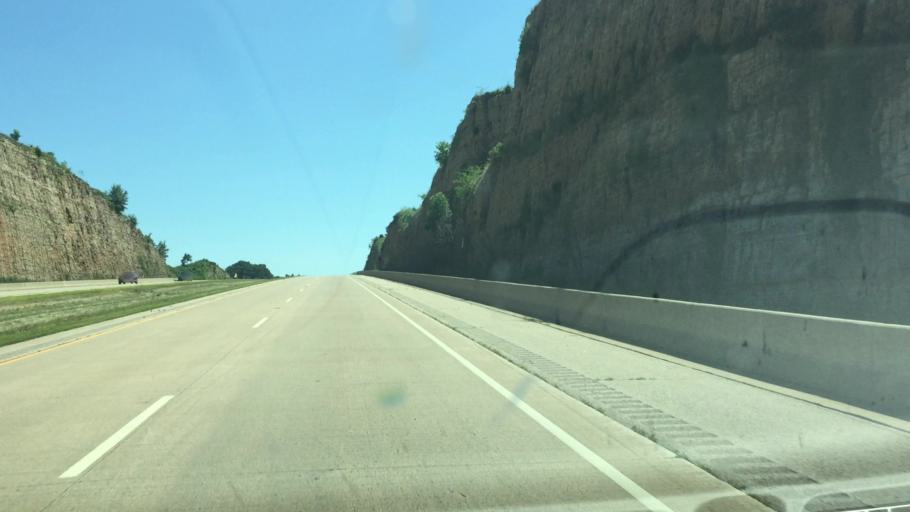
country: US
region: Wisconsin
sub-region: Grant County
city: Dickeyville
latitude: 42.6382
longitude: -90.5787
